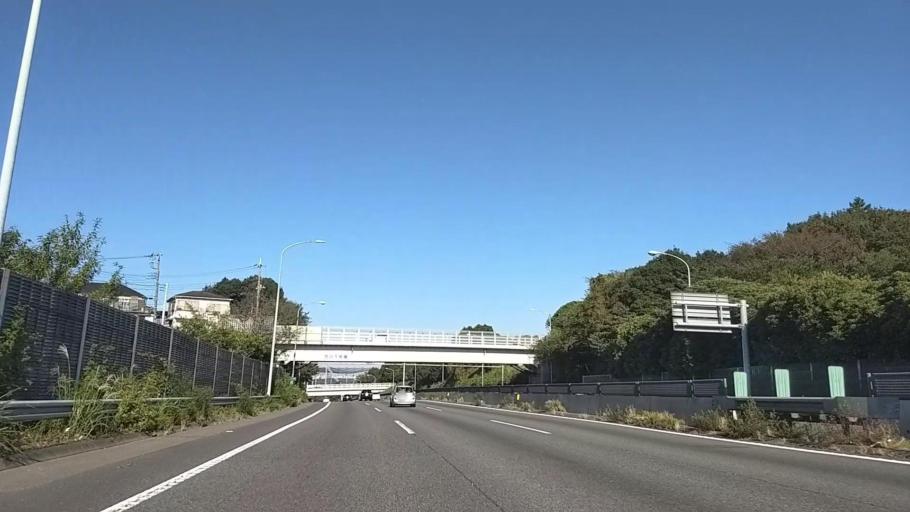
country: JP
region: Kanagawa
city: Minami-rinkan
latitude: 35.4723
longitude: 139.5313
